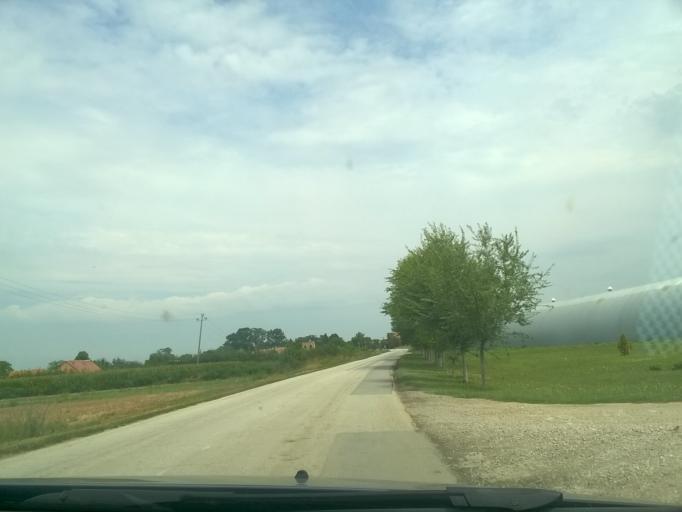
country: RS
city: Boka
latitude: 45.3472
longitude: 20.8251
